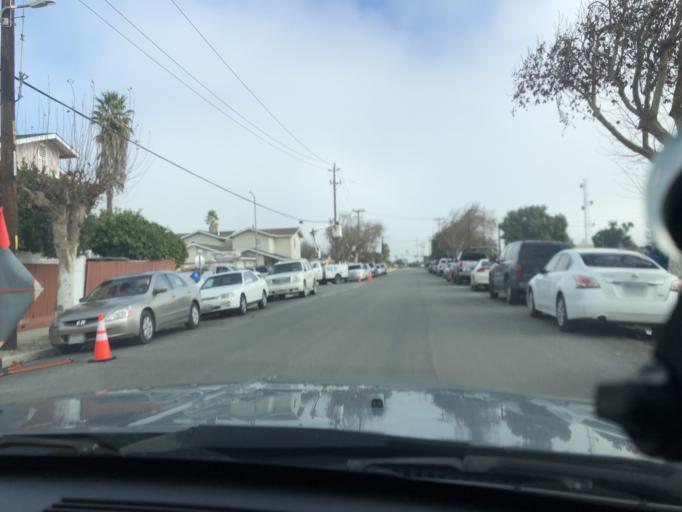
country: US
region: California
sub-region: Monterey County
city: King City
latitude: 36.2180
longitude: -121.1302
